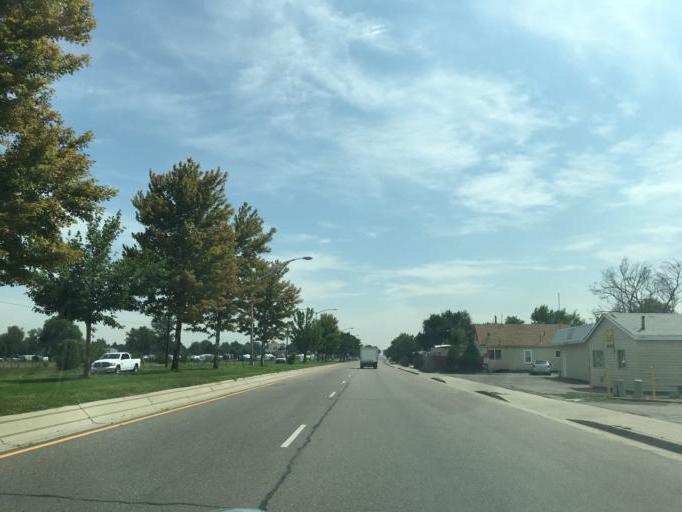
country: US
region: Colorado
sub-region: Adams County
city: Aurora
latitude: 39.7401
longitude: -104.8053
